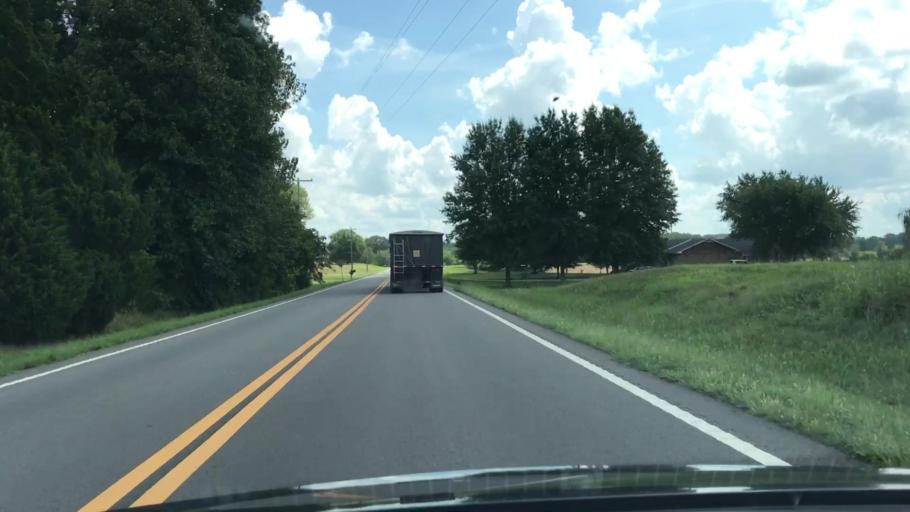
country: US
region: Tennessee
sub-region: Robertson County
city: Springfield
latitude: 36.6219
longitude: -86.9479
